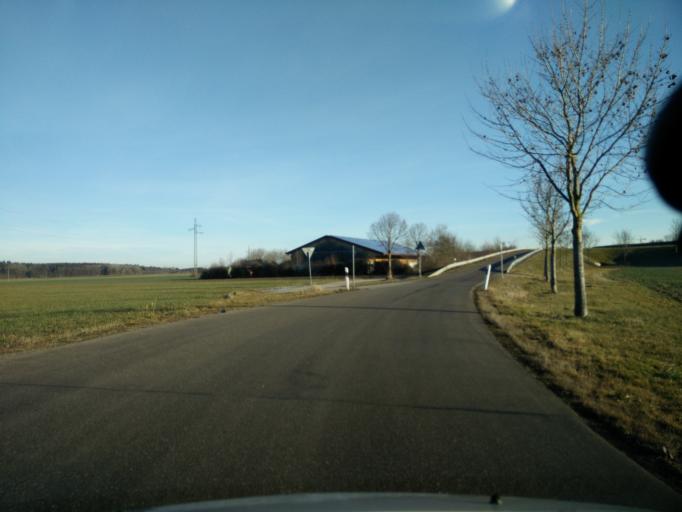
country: DE
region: Bavaria
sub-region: Upper Bavaria
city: Germering
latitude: 48.1483
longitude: 11.3913
